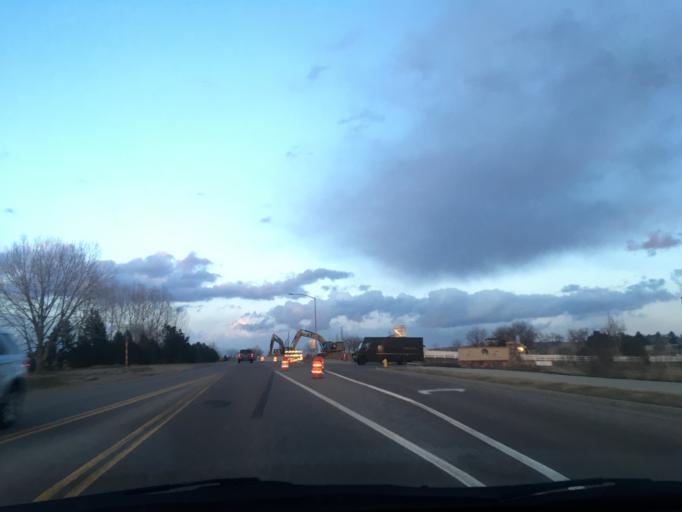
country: US
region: Colorado
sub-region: Adams County
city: Todd Creek
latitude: 39.9574
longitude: -104.9475
